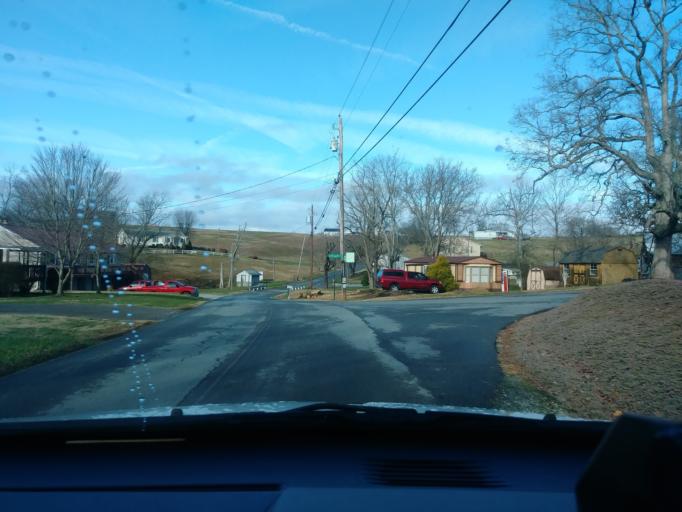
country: US
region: Tennessee
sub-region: Greene County
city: Mosheim
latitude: 36.0921
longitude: -82.9177
